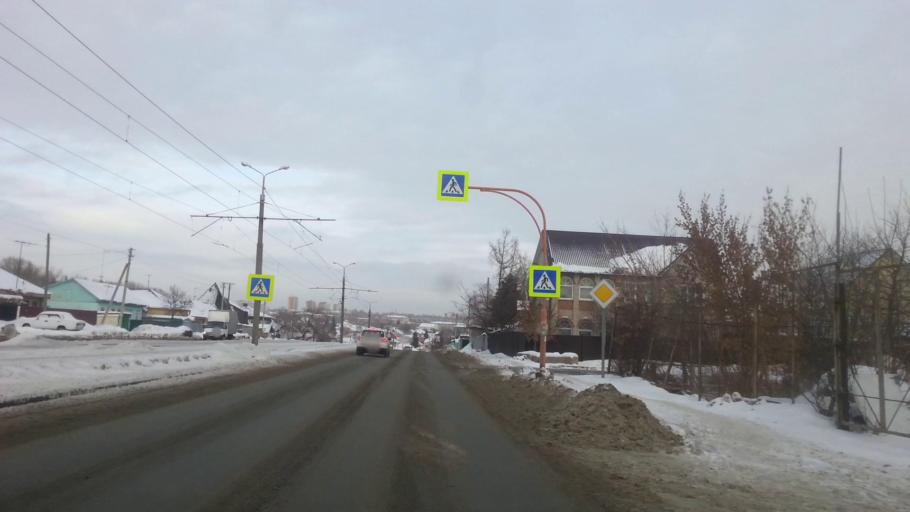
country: RU
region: Altai Krai
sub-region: Gorod Barnaulskiy
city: Barnaul
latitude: 53.3637
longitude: 83.7295
